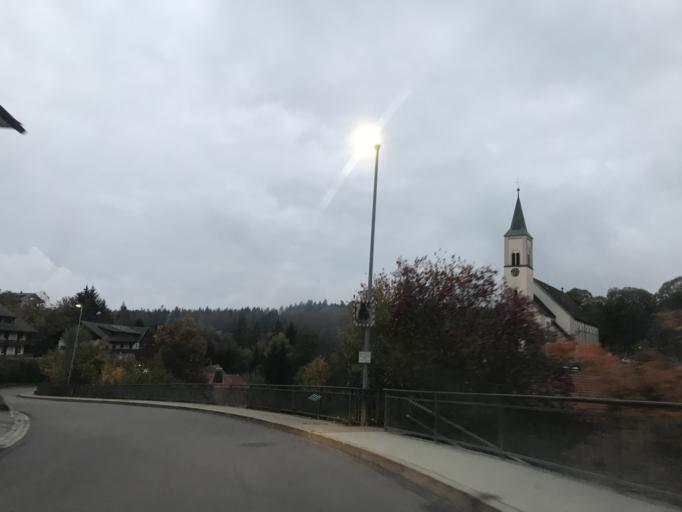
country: DE
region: Baden-Wuerttemberg
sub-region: Freiburg Region
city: Rickenbach
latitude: 47.6199
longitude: 7.9801
